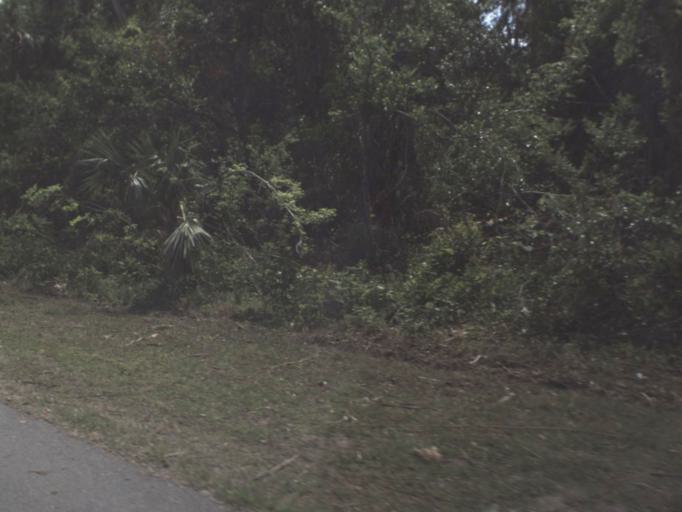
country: US
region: Florida
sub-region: Flagler County
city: Palm Coast
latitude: 29.5796
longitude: -81.1877
